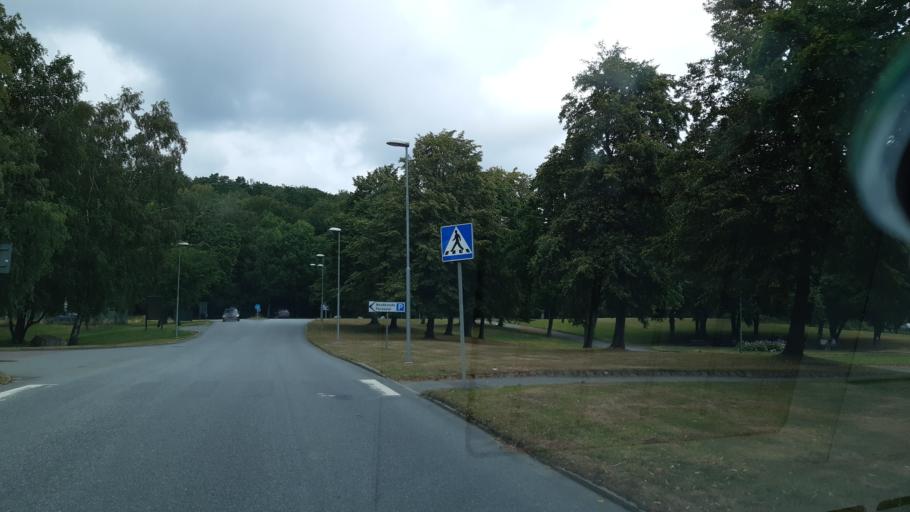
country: SE
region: Vaestra Goetaland
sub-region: Goteborg
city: Eriksbo
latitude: 57.7224
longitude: 12.0497
